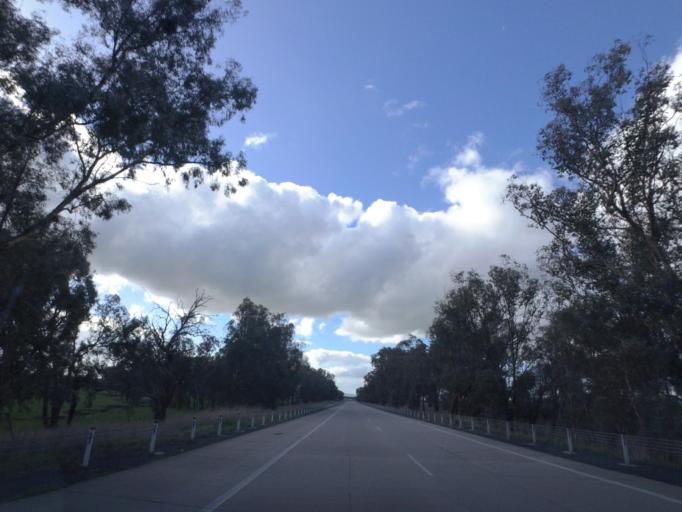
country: AU
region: New South Wales
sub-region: Greater Hume Shire
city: Holbrook
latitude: -35.7453
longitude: 147.3002
